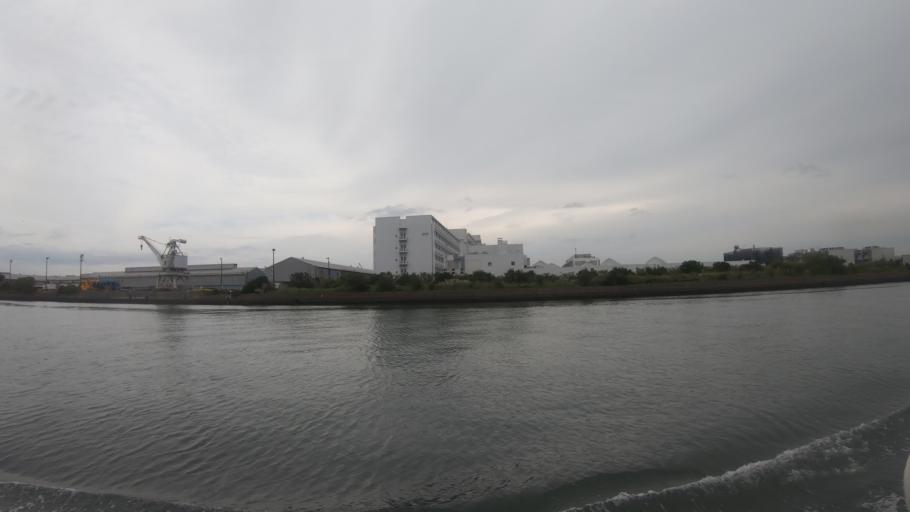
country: JP
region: Kanagawa
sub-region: Kawasaki-shi
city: Kawasaki
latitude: 35.4881
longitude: 139.6793
